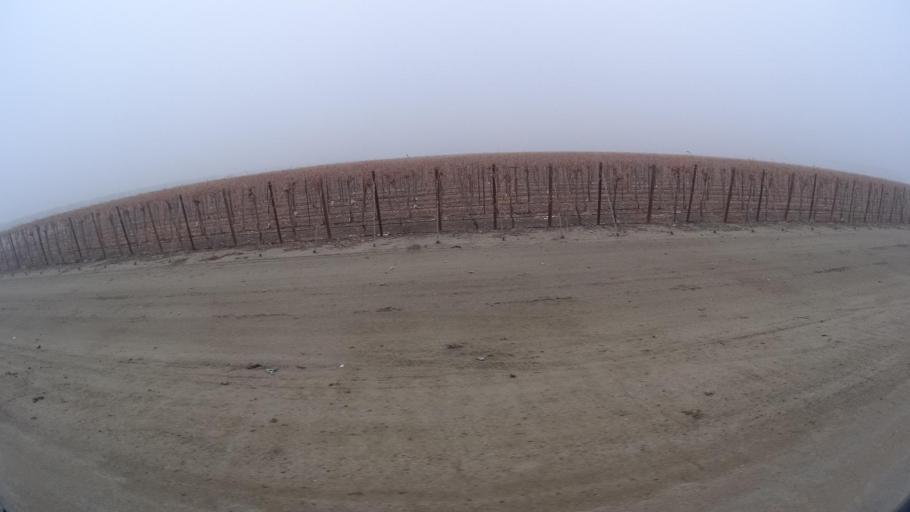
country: US
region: California
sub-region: Kern County
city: Buttonwillow
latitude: 35.4550
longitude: -119.5650
